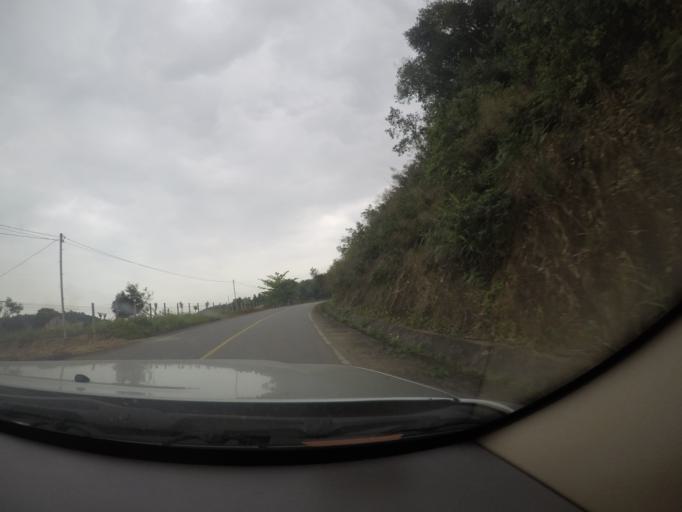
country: VN
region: Quang Binh
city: Hoan Lao
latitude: 17.6142
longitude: 106.4024
